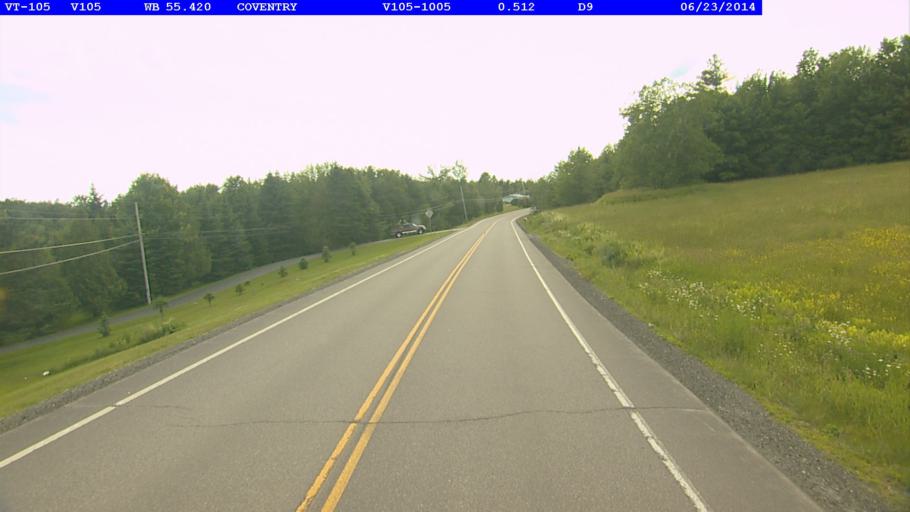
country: US
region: Vermont
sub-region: Orleans County
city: Newport
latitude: 44.9296
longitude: -72.2580
